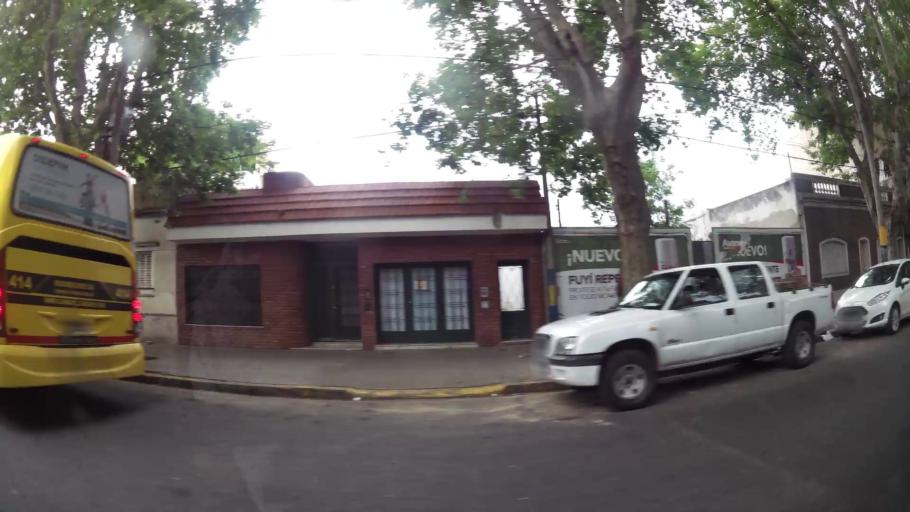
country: AR
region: Santa Fe
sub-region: Departamento de Rosario
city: Rosario
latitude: -32.9151
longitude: -60.6801
